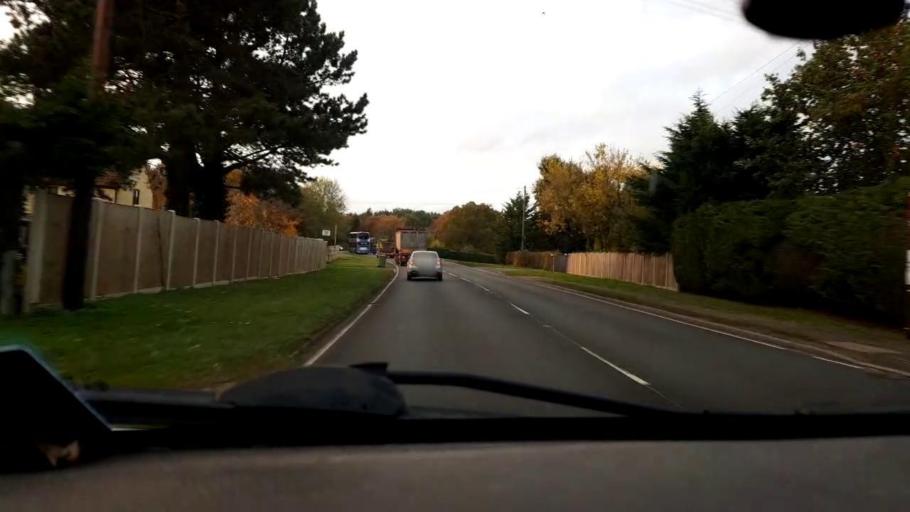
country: GB
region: England
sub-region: Norfolk
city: Costessey
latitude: 52.7105
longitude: 1.1405
